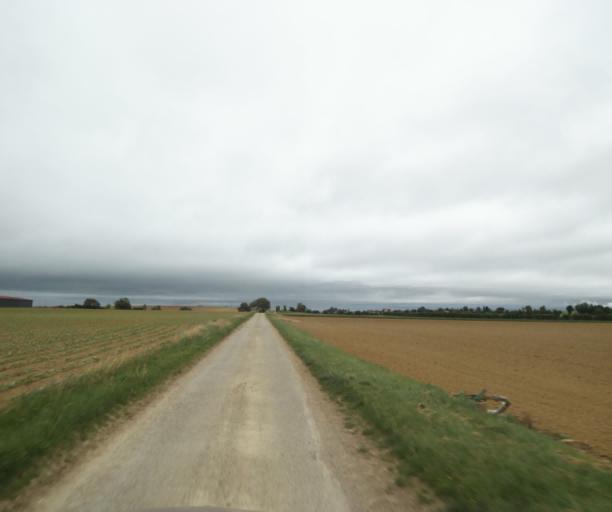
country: FR
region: Rhone-Alpes
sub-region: Departement de l'Ain
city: Miribel
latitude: 45.8353
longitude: 4.9346
